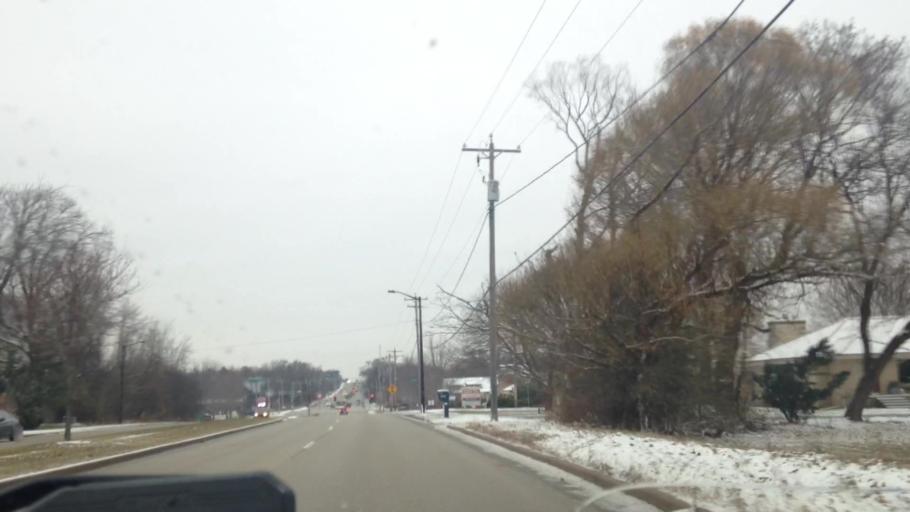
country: US
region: Wisconsin
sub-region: Waukesha County
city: Butler
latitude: 43.1166
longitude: -88.1053
